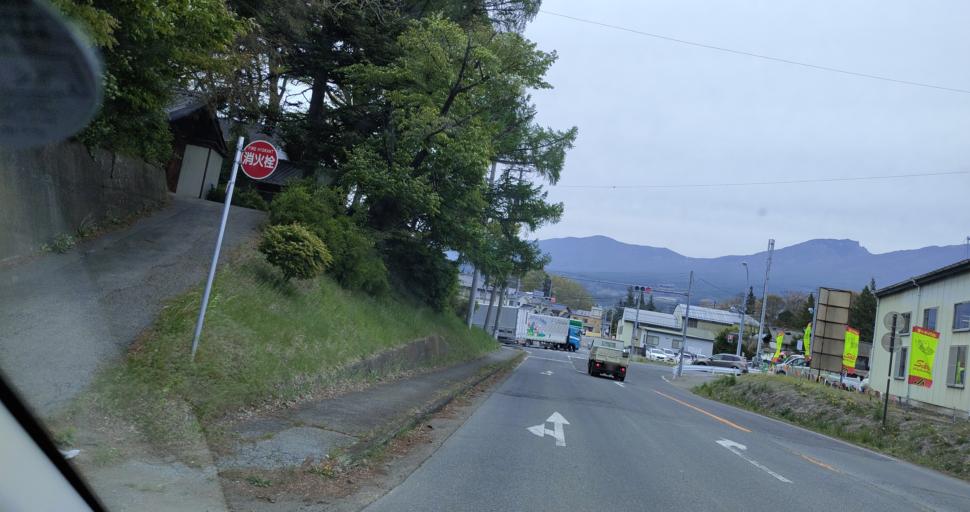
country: JP
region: Nagano
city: Komoro
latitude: 36.3197
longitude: 138.4935
